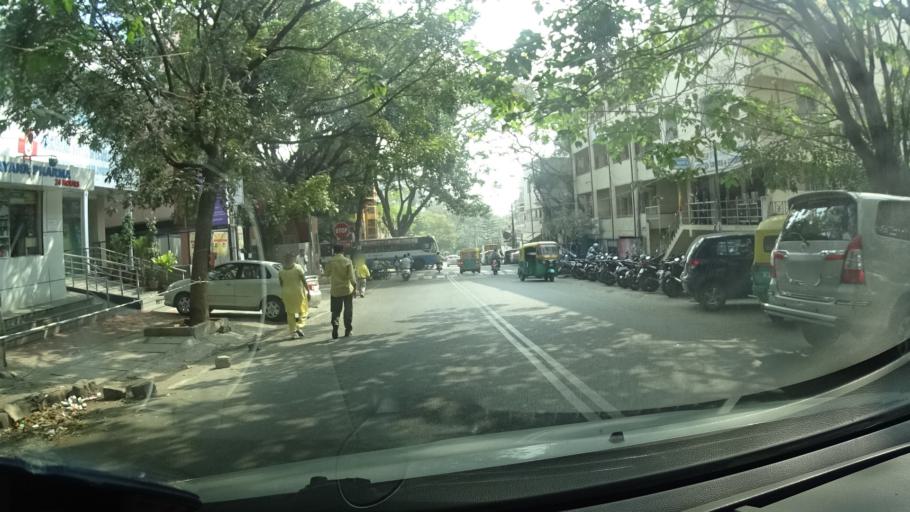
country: IN
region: Karnataka
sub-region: Bangalore Urban
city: Bangalore
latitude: 13.0001
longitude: 77.5689
